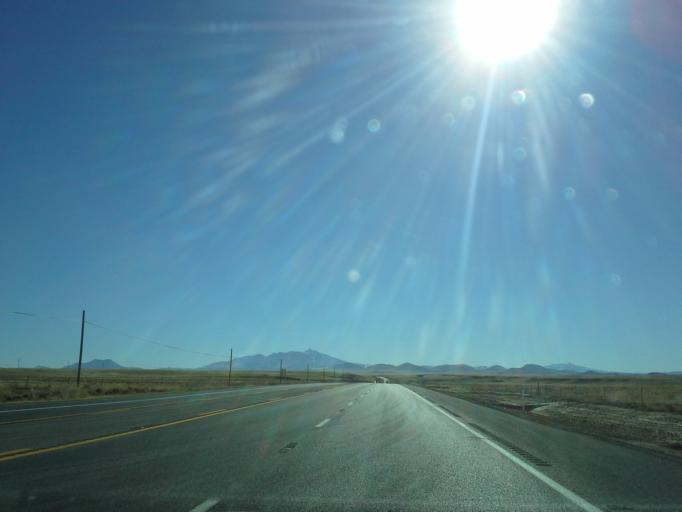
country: US
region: Arizona
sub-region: Coconino County
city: Tuba City
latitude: 35.7164
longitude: -111.4881
